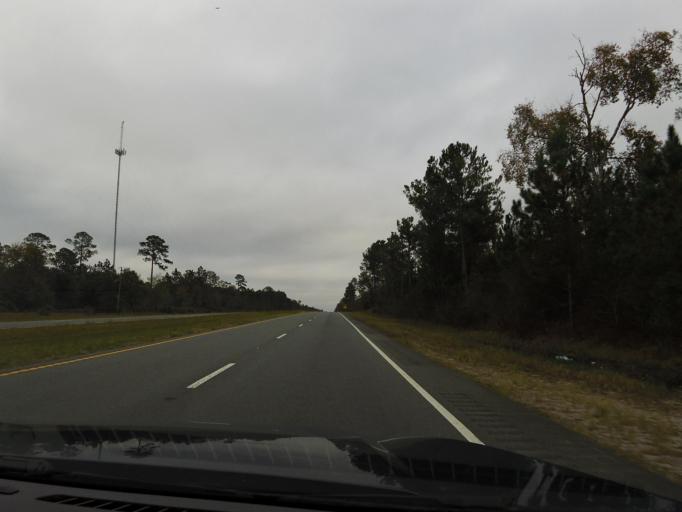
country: US
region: Georgia
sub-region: Charlton County
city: Folkston
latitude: 30.9057
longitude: -82.0692
